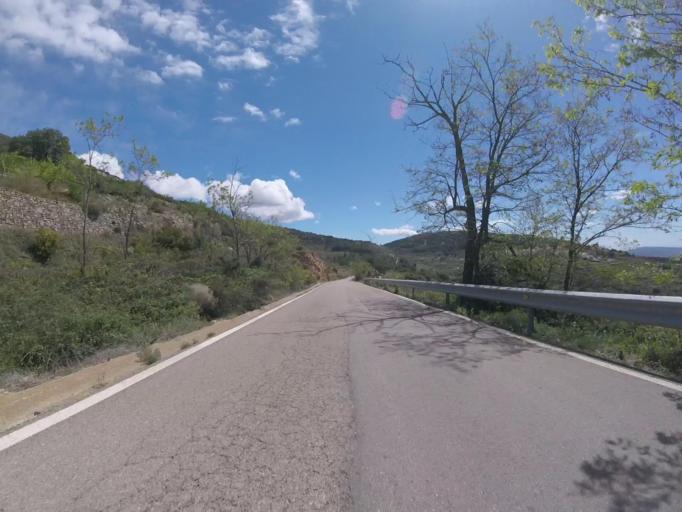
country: ES
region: Valencia
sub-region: Provincia de Castello
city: Sierra-Engarceran
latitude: 40.2755
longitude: -0.0279
